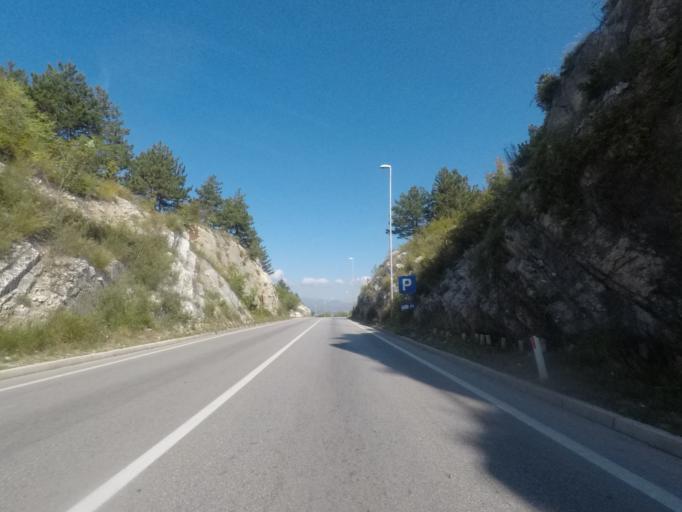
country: ME
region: Opstina Niksic
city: Niksic
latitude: 42.7710
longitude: 18.9406
